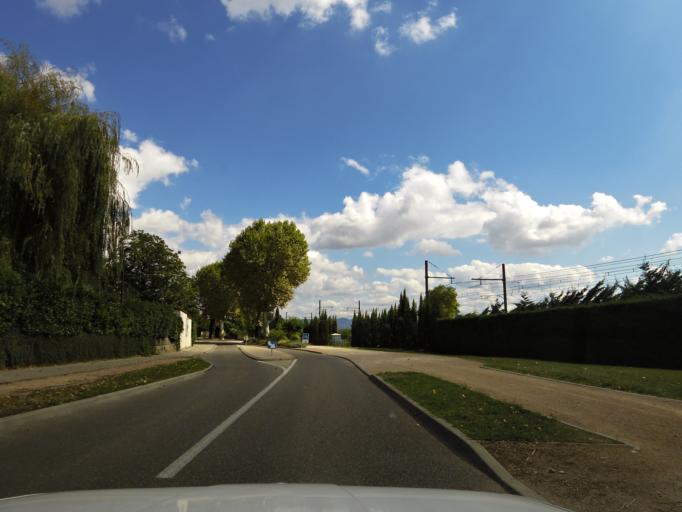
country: FR
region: Rhone-Alpes
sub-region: Departement de l'Ain
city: Meximieux
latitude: 45.9050
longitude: 5.2015
